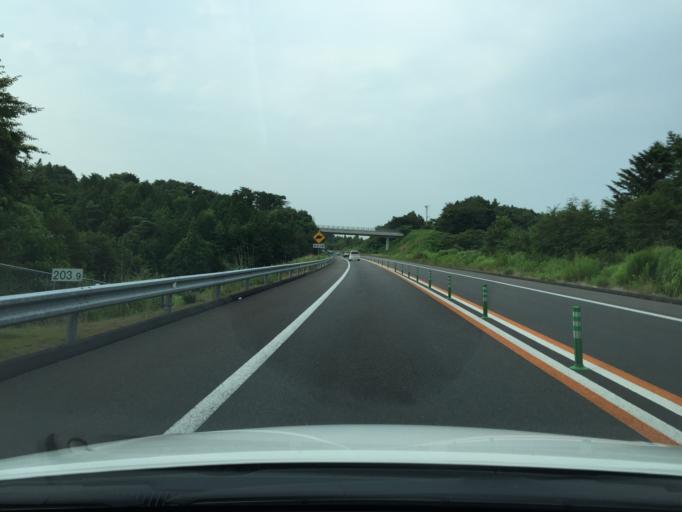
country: JP
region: Fukushima
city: Iwaki
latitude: 37.2528
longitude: 140.9910
